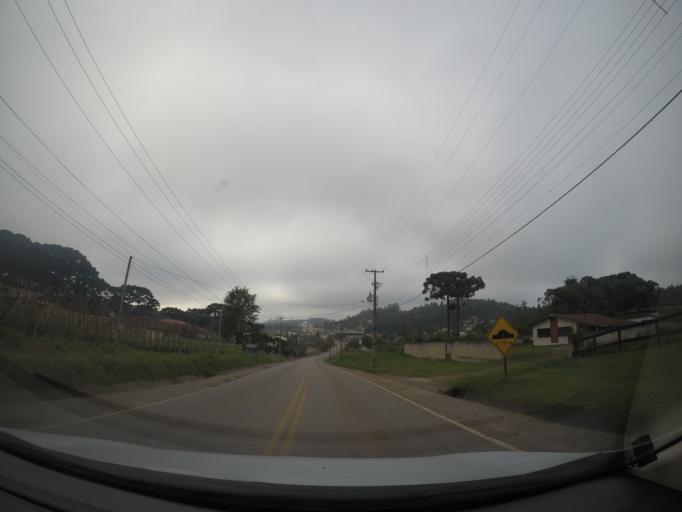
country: BR
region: Parana
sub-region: Colombo
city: Colombo
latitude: -25.2930
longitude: -49.2484
